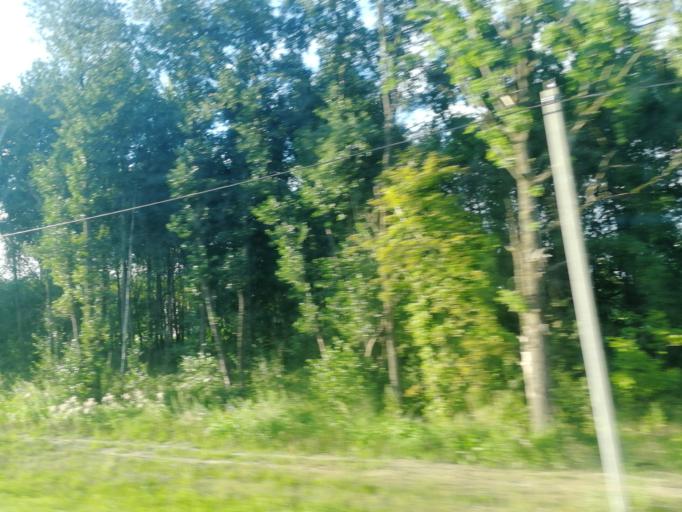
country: RU
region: Kaluga
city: Kaluga
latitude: 54.4390
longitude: 36.3354
